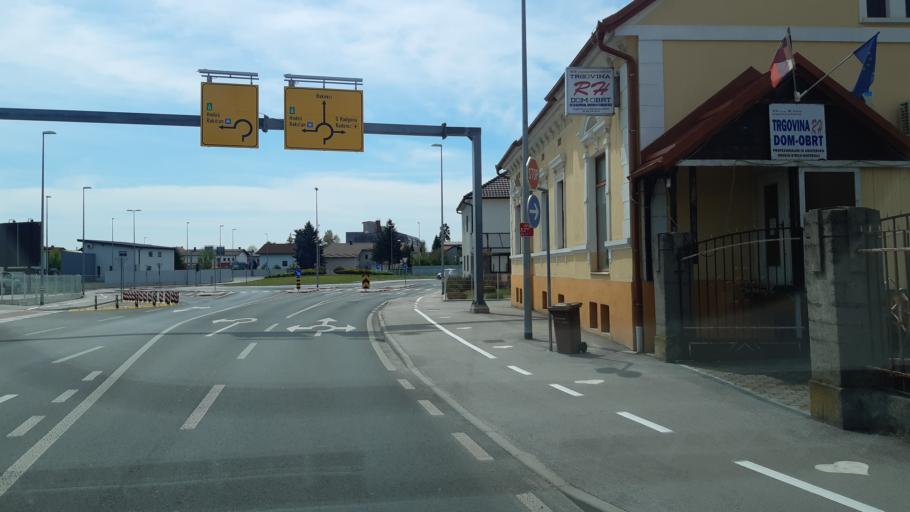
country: SI
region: Murska Sobota
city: Murska Sobota
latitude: 46.6574
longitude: 16.1692
